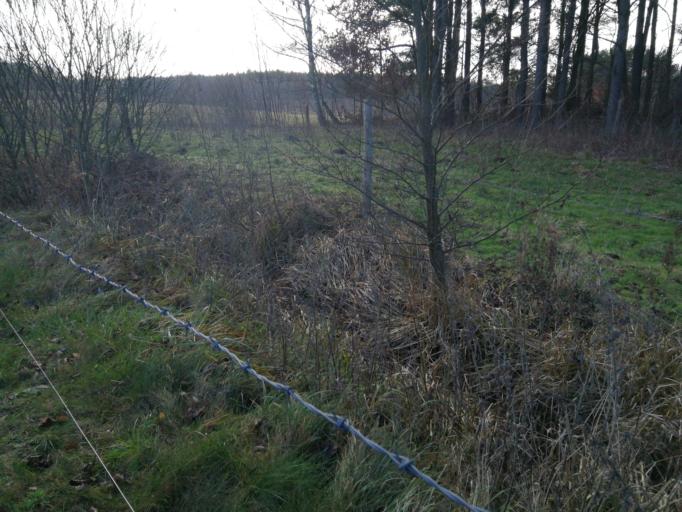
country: PL
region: Warmian-Masurian Voivodeship
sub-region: Powiat dzialdowski
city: Rybno
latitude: 53.4125
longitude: 19.9082
